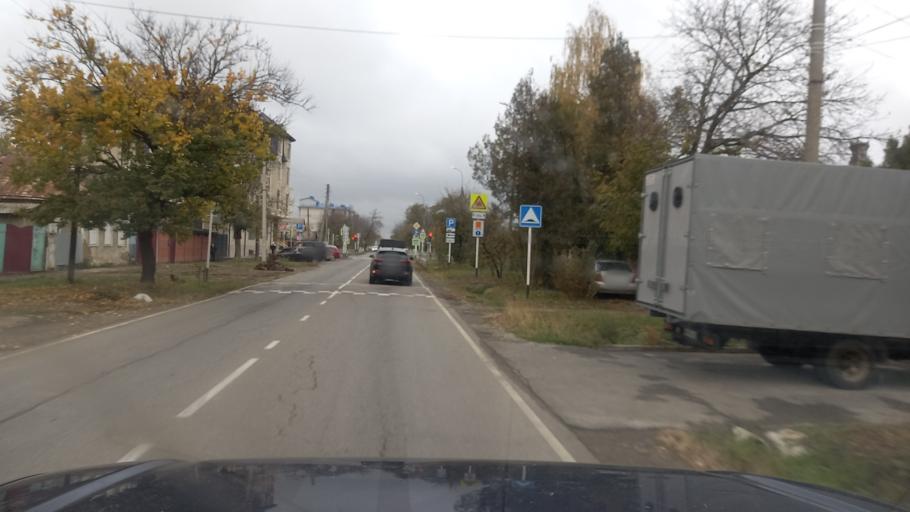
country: RU
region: Adygeya
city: Maykop
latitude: 44.6069
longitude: 40.0717
